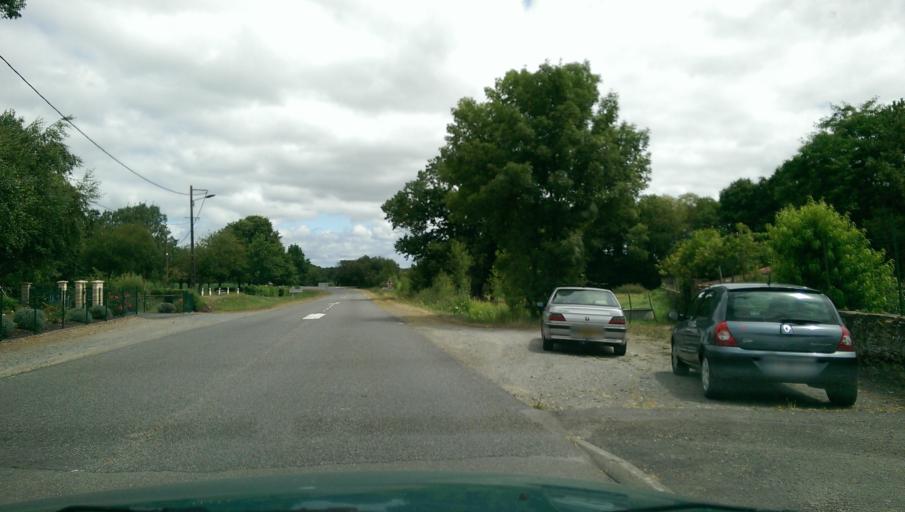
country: FR
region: Pays de la Loire
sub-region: Departement de la Loire-Atlantique
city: Vieillevigne
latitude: 46.9747
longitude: -1.4346
